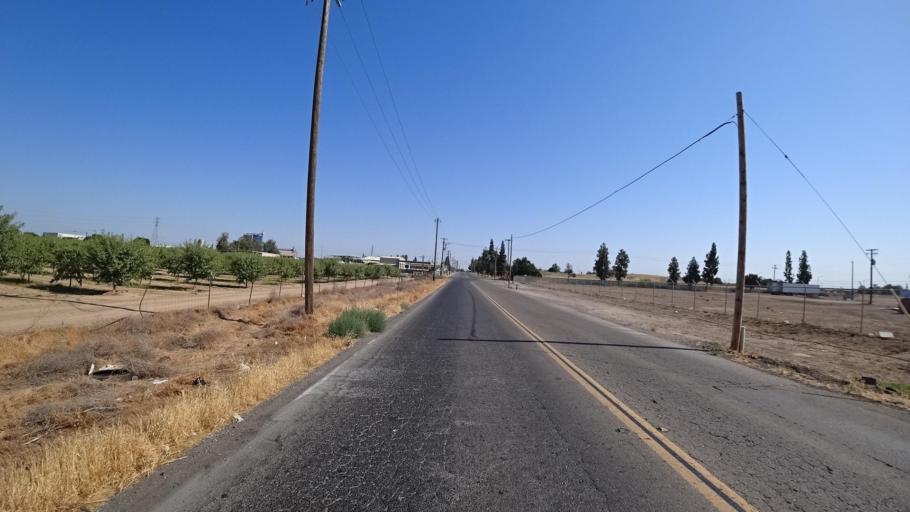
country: US
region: California
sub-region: Fresno County
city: West Park
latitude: 36.7129
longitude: -119.8180
